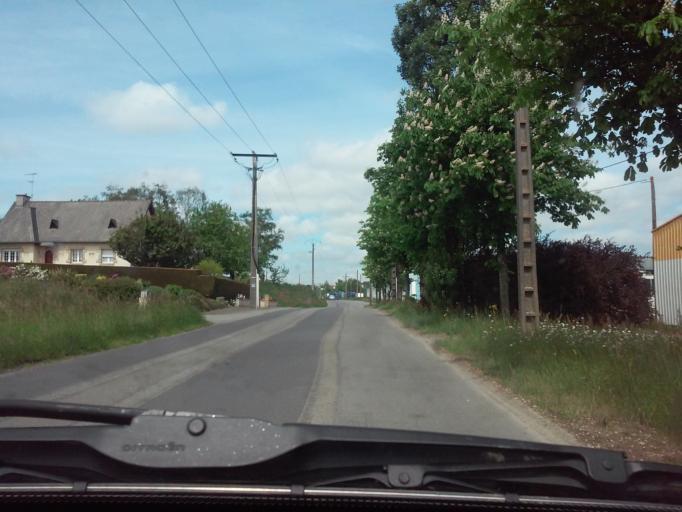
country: FR
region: Brittany
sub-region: Departement d'Ille-et-Vilaine
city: Beauce
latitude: 48.3314
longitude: -1.1640
